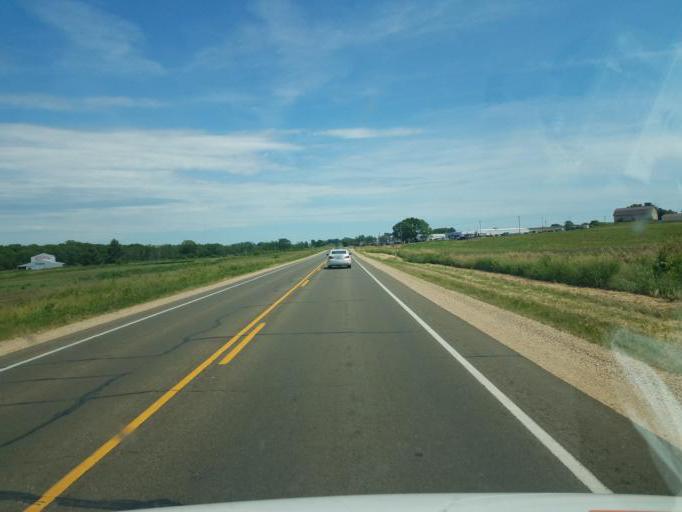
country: US
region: Wisconsin
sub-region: Sauk County
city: Reedsburg
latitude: 43.5490
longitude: -90.0565
